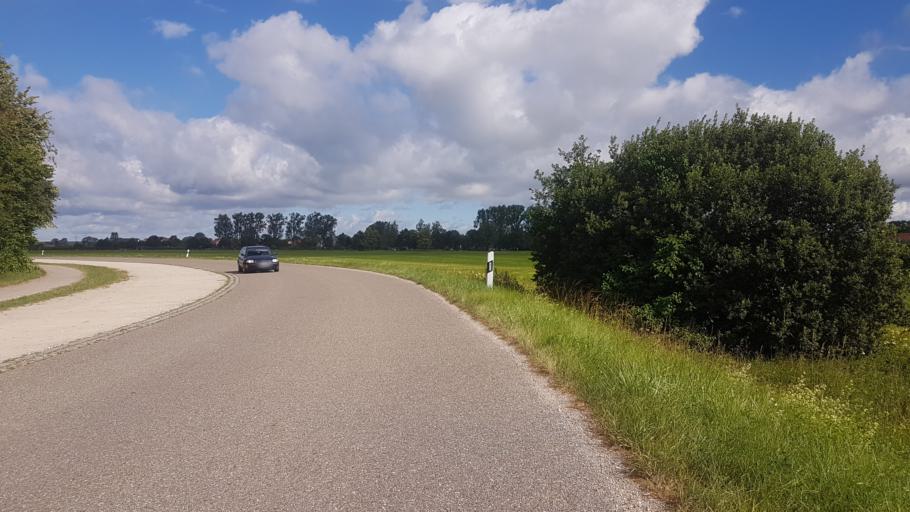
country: DE
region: Bavaria
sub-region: Regierungsbezirk Mittelfranken
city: Ornbau
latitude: 49.1696
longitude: 10.6584
